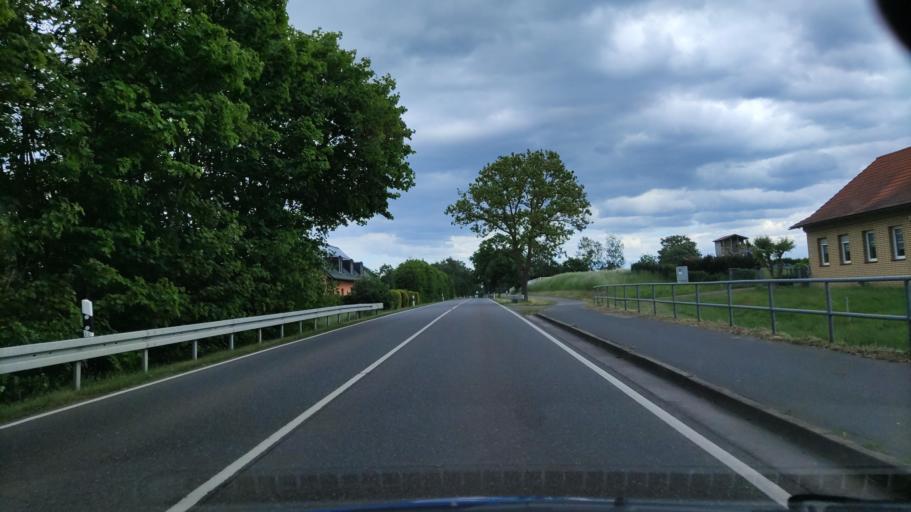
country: DE
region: Mecklenburg-Vorpommern
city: Lubz
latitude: 53.4663
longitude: 12.0706
